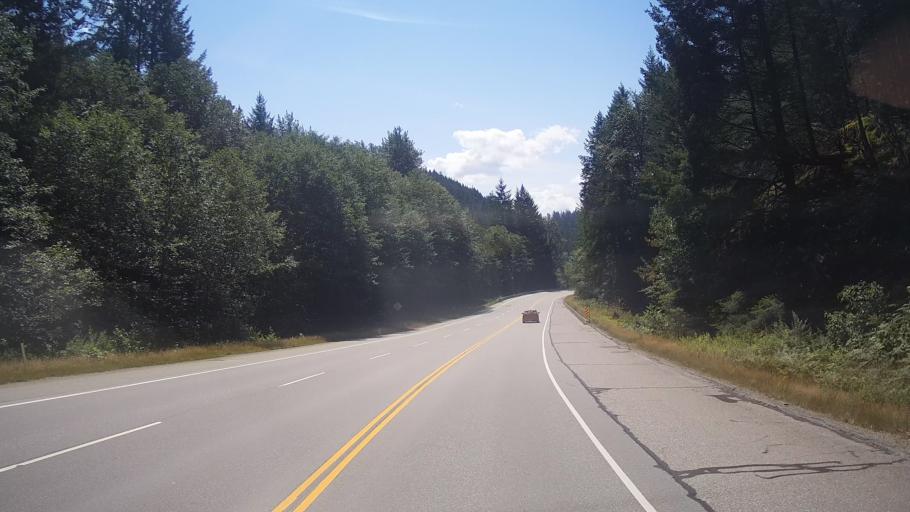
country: CA
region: British Columbia
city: Whistler
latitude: 49.8133
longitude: -123.1223
